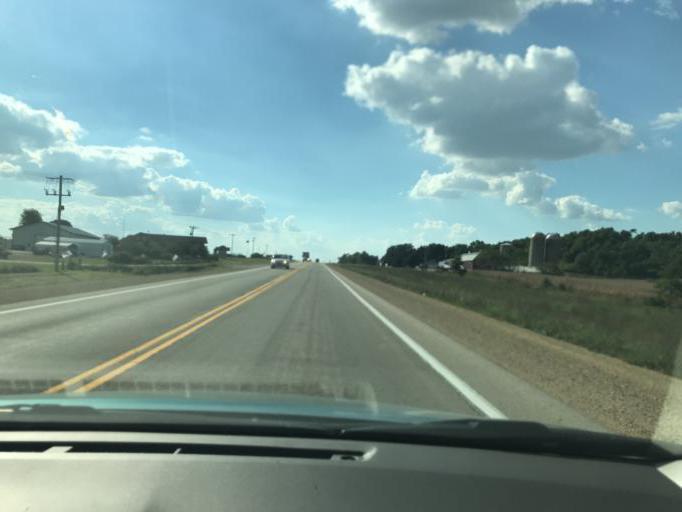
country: US
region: Wisconsin
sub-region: Green County
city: Brodhead
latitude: 42.5880
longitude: -89.4161
